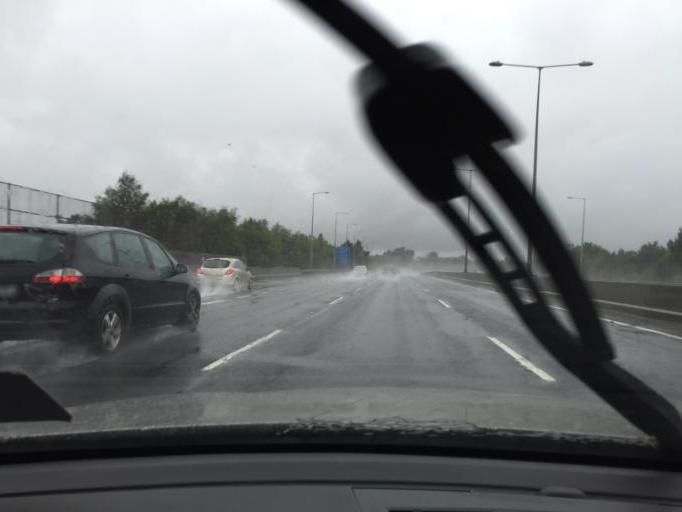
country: IE
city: Cherry Orchard
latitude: 53.3334
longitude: -6.3831
